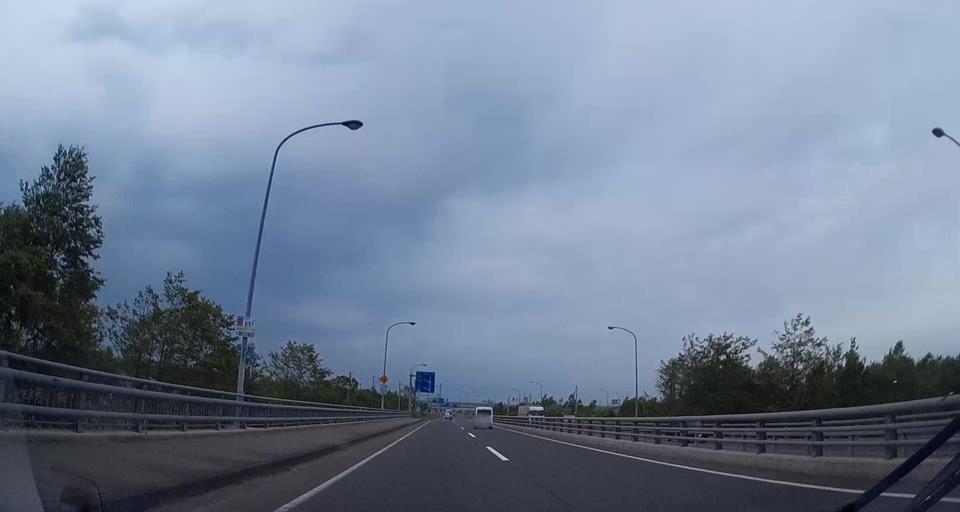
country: JP
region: Hokkaido
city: Tomakomai
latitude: 42.6802
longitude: 141.7157
